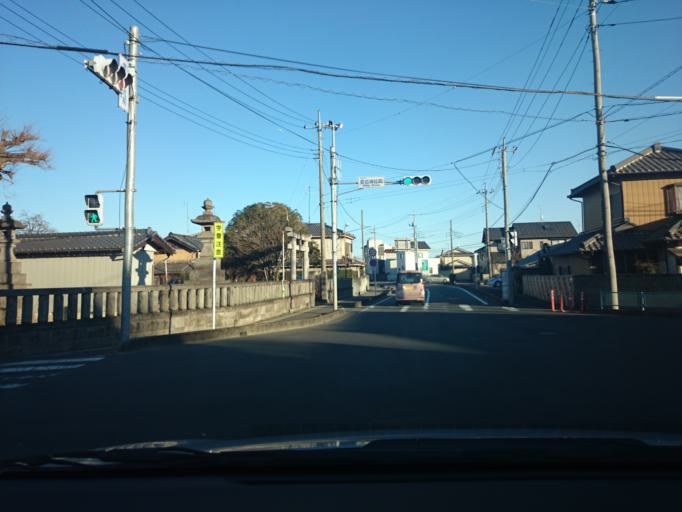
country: JP
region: Saitama
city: Hanyu
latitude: 36.1818
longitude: 139.5051
